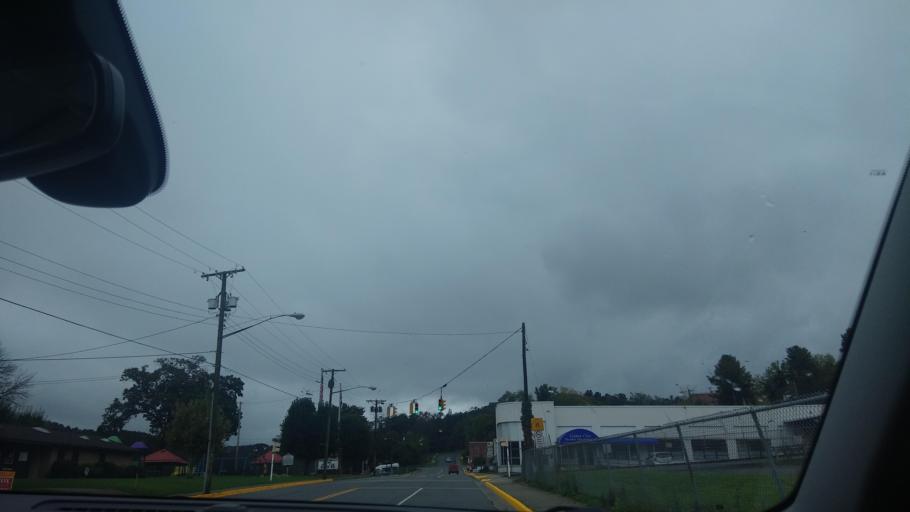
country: US
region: Virginia
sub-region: City of Galax
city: Galax
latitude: 36.6583
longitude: -80.9233
